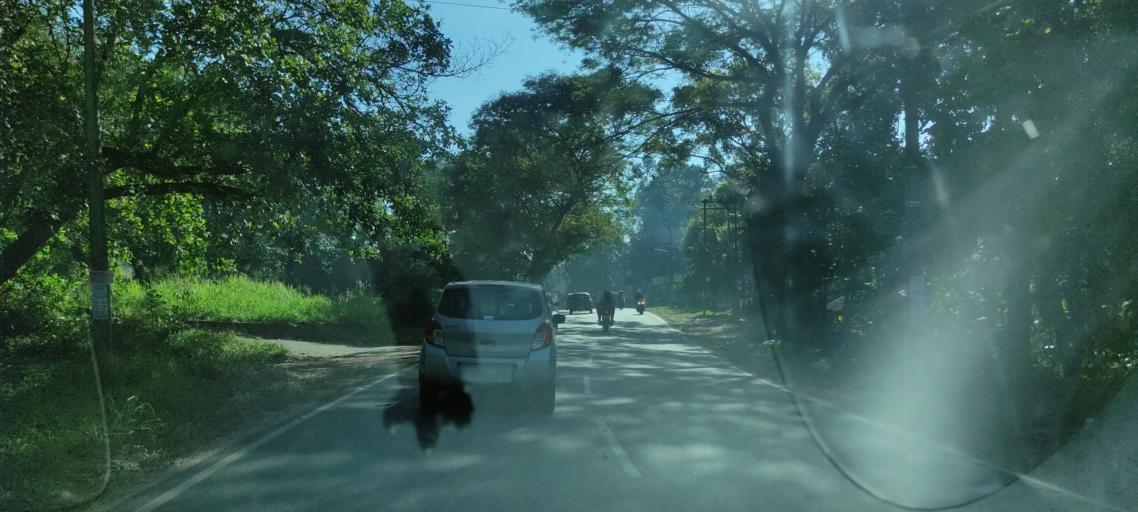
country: IN
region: Kerala
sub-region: Pattanamtitta
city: Adur
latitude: 9.1637
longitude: 76.6991
